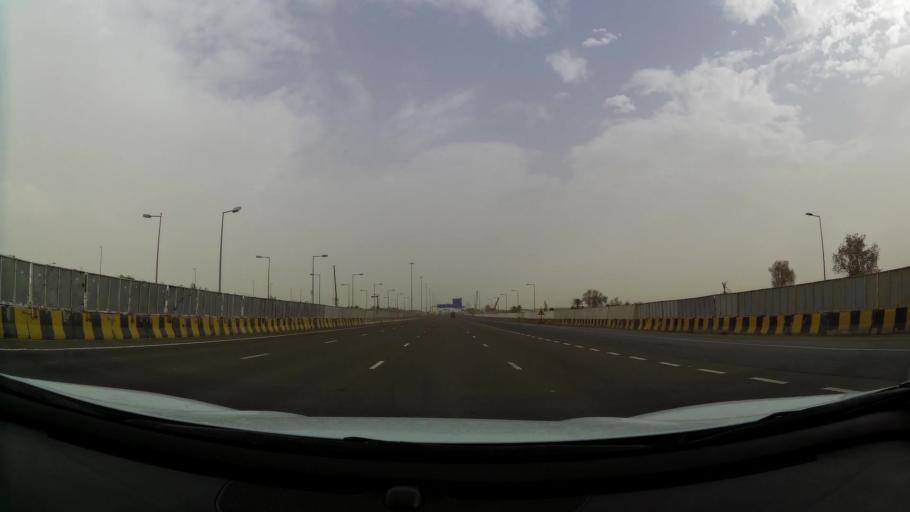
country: AE
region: Abu Dhabi
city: Abu Dhabi
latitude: 24.4702
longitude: 54.6328
